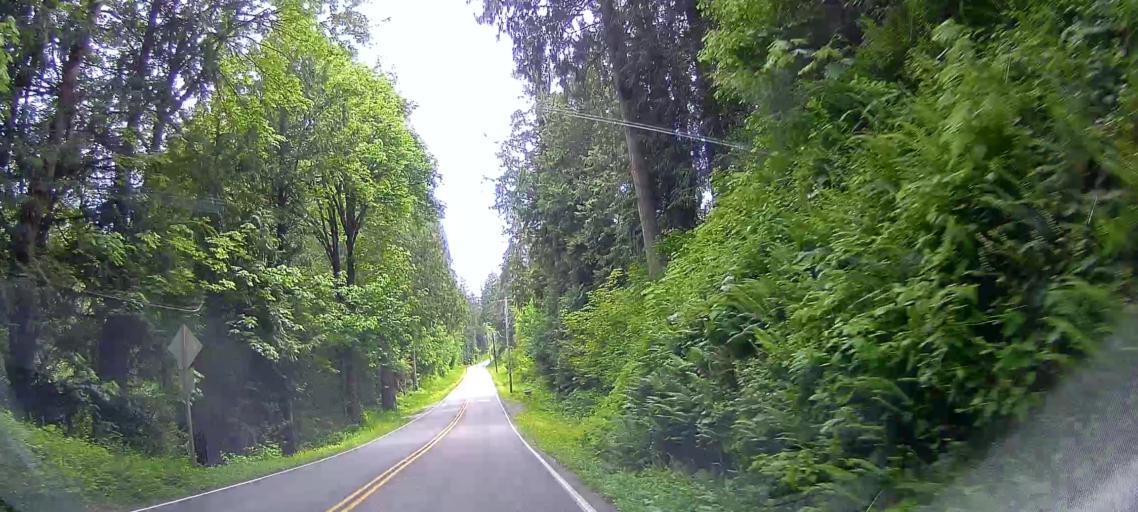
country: US
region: Washington
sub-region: Snohomish County
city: Bryant
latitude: 48.2390
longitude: -122.1985
